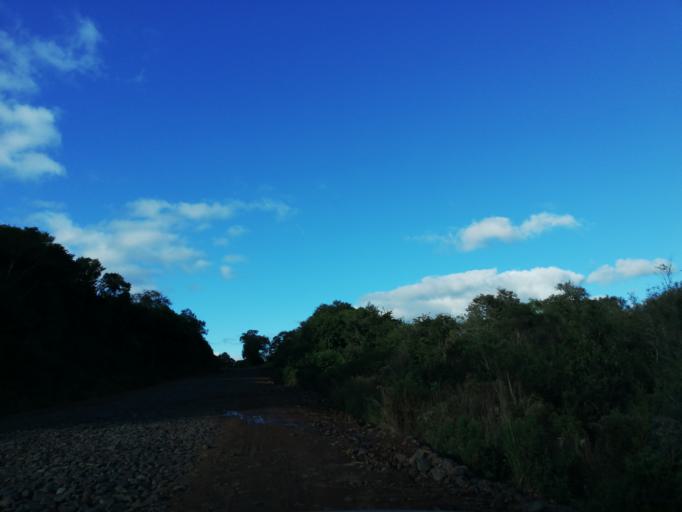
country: AR
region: Misiones
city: Almafuerte
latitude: -27.5517
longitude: -55.4173
